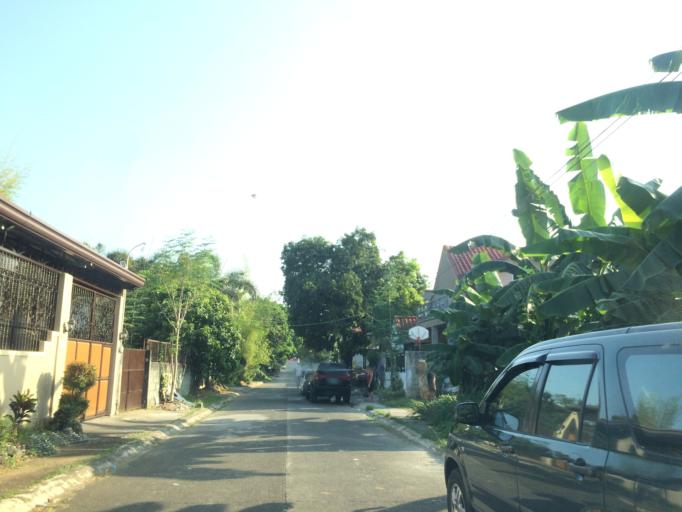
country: PH
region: Calabarzon
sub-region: Province of Rizal
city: San Mateo
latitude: 14.6718
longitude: 121.1224
